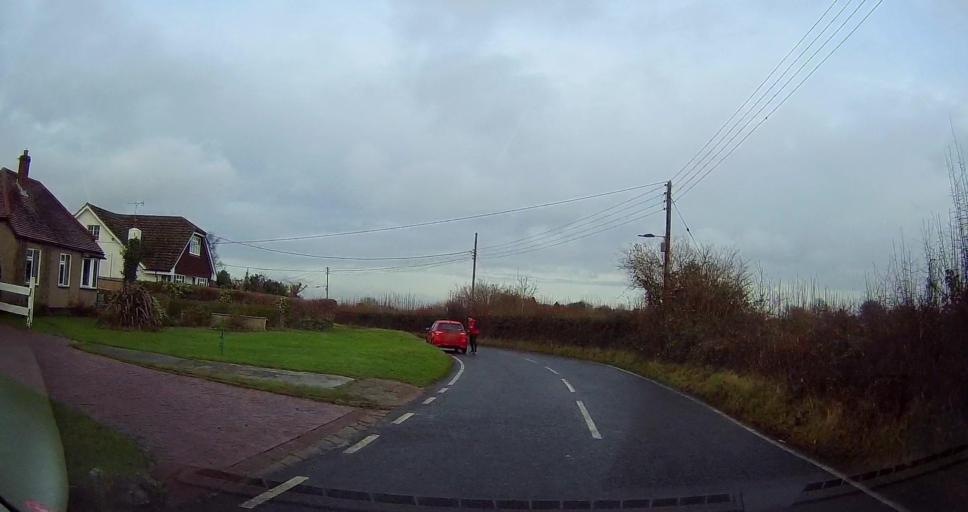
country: GB
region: England
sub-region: Kent
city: Biggin Hill
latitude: 51.3331
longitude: 0.0753
